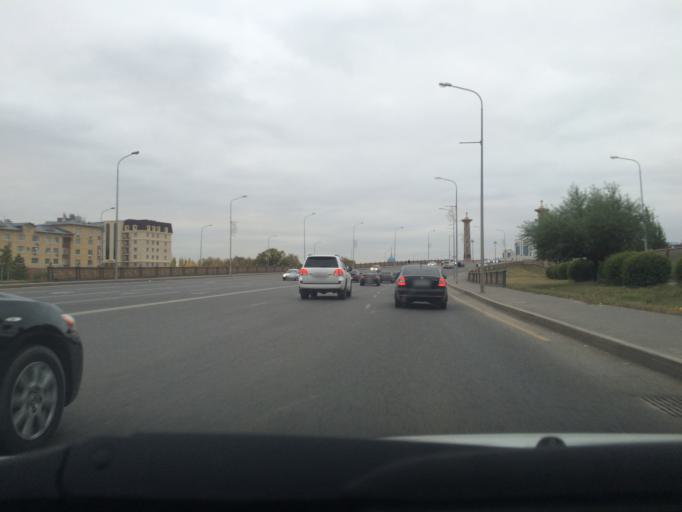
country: KZ
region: Astana Qalasy
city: Astana
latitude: 51.1416
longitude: 71.4450
